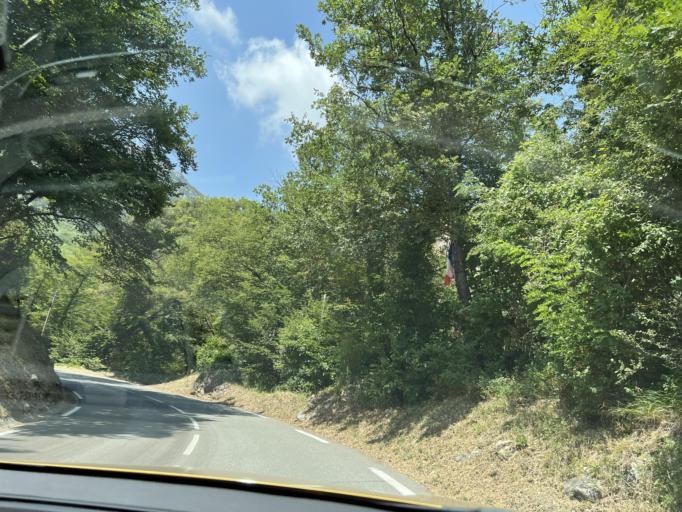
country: FR
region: Provence-Alpes-Cote d'Azur
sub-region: Departement des Alpes-Maritimes
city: Tourrettes-sur-Loup
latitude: 43.7506
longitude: 6.9963
